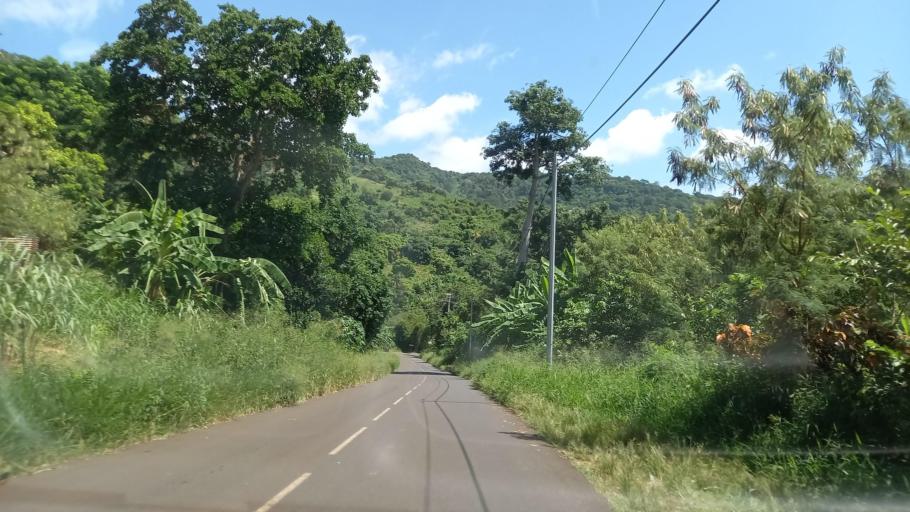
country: YT
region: Bandraboua
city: Bandraboua
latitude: -12.6852
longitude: 45.1011
